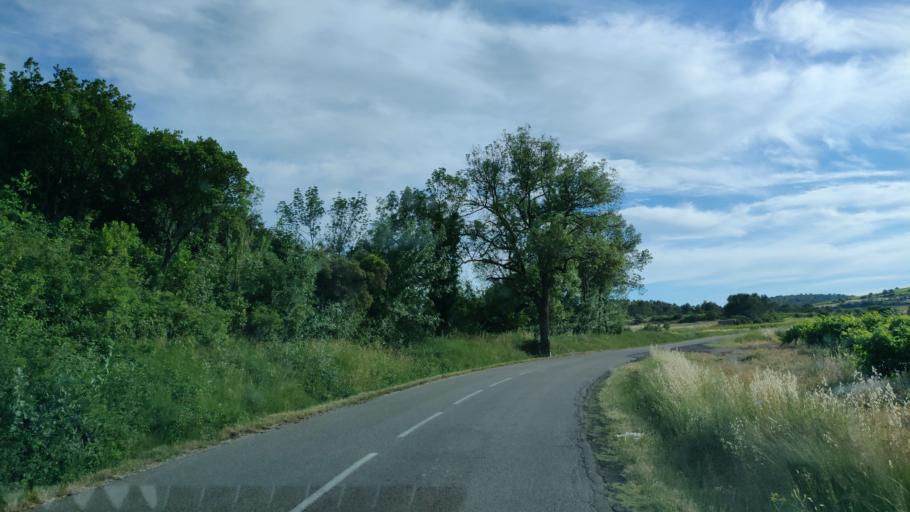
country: FR
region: Languedoc-Roussillon
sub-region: Departement de l'Herault
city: Combaillaux
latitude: 43.6645
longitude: 3.7783
